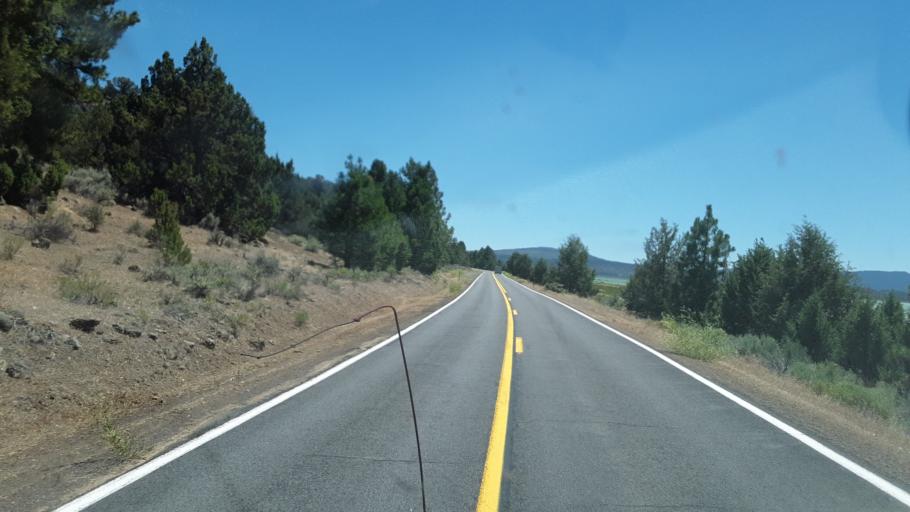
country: US
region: California
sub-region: Lassen County
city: Susanville
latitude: 40.7044
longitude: -120.6728
